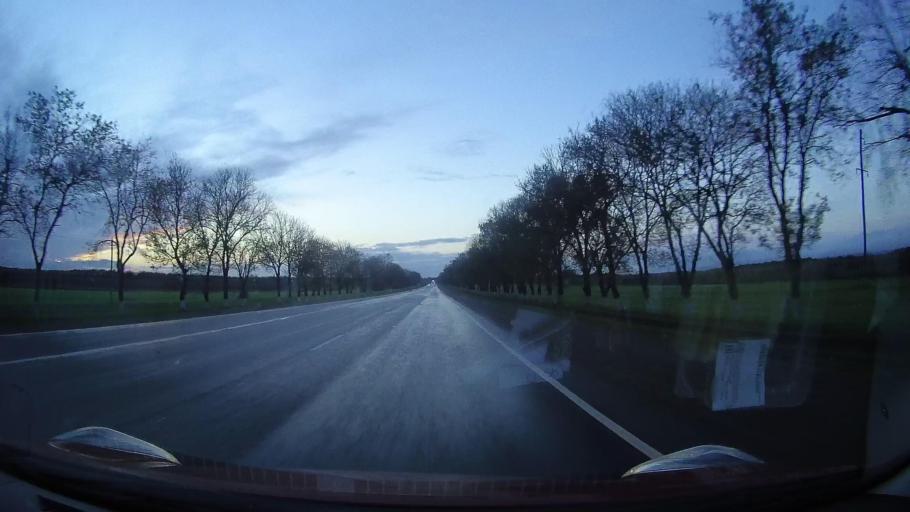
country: RU
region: Krasnodarskiy
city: Uspenskoye
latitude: 44.8235
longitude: 41.3563
